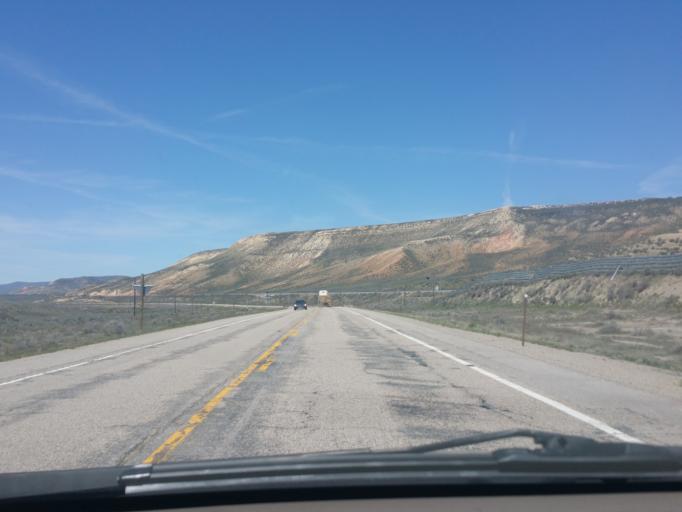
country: US
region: Wyoming
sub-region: Lincoln County
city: Kemmerer
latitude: 41.8134
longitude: -110.6258
